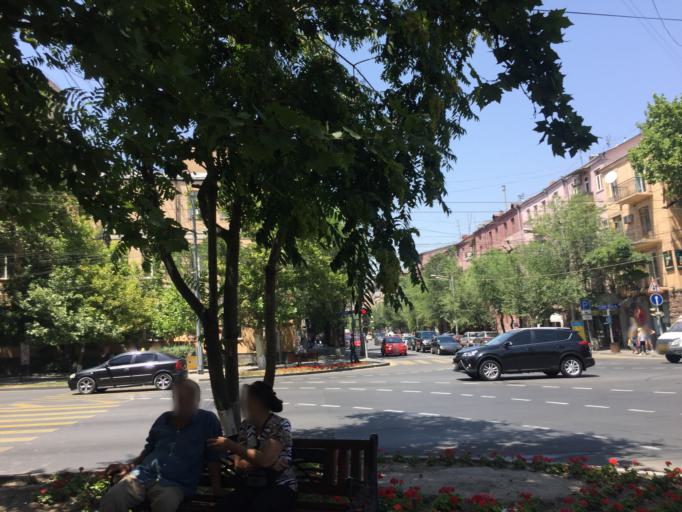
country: AM
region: Yerevan
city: Yerevan
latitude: 40.1855
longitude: 44.5131
